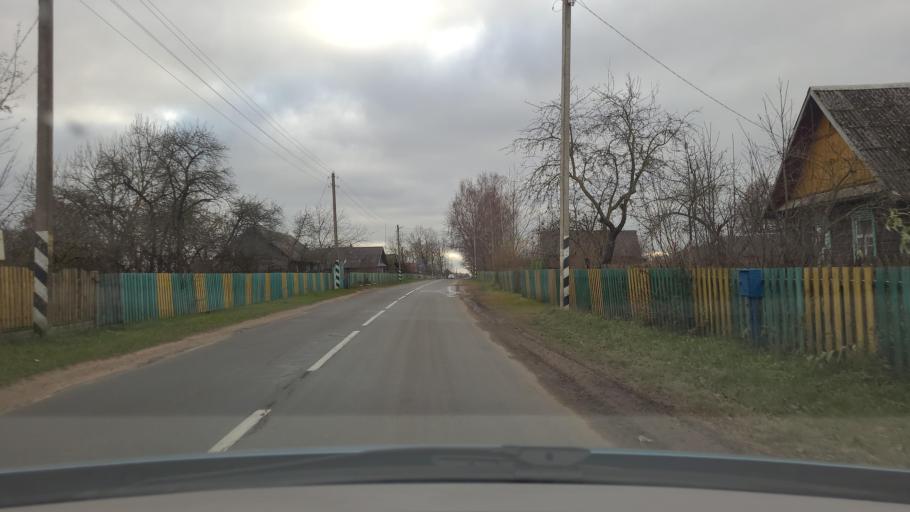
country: BY
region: Minsk
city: Khalopyenichy
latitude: 54.4558
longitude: 28.9846
